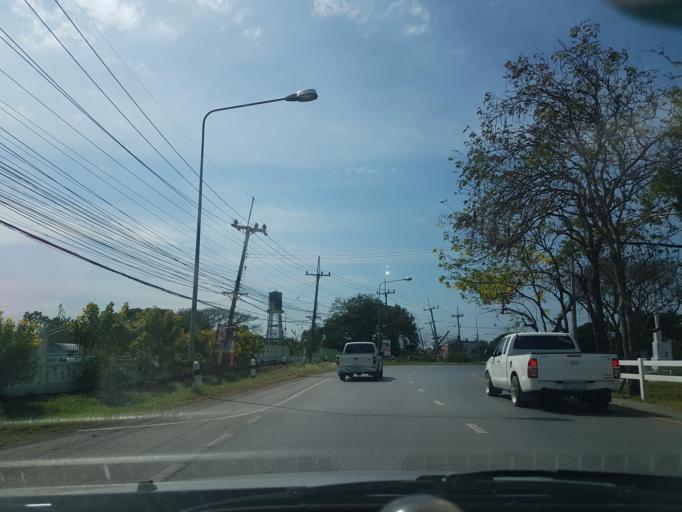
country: TH
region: Lop Buri
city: Lop Buri
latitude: 14.7967
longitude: 100.7132
